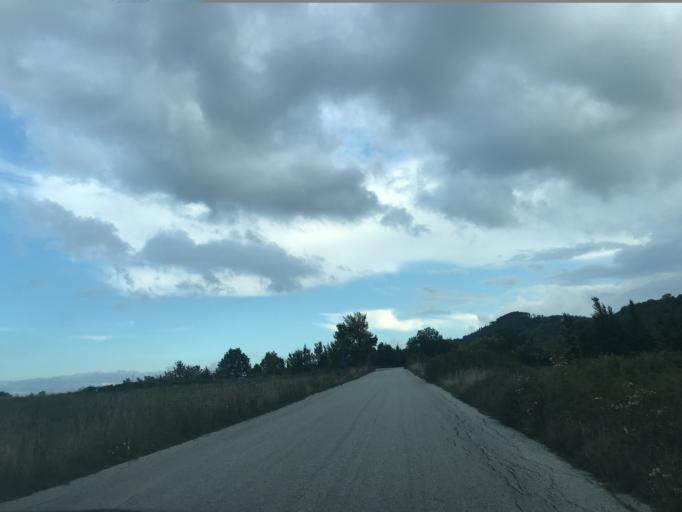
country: IT
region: Molise
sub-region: Provincia di Campobasso
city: Duronia
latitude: 41.6717
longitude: 14.4604
